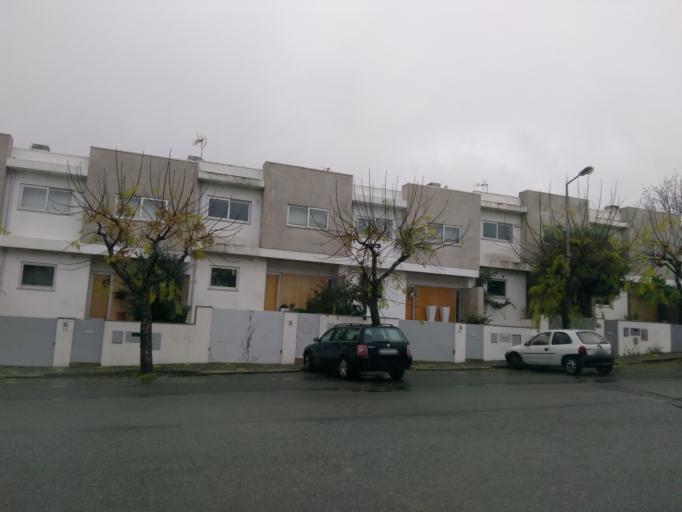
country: PT
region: Braga
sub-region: Braga
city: Adaufe
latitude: 41.5698
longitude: -8.3773
